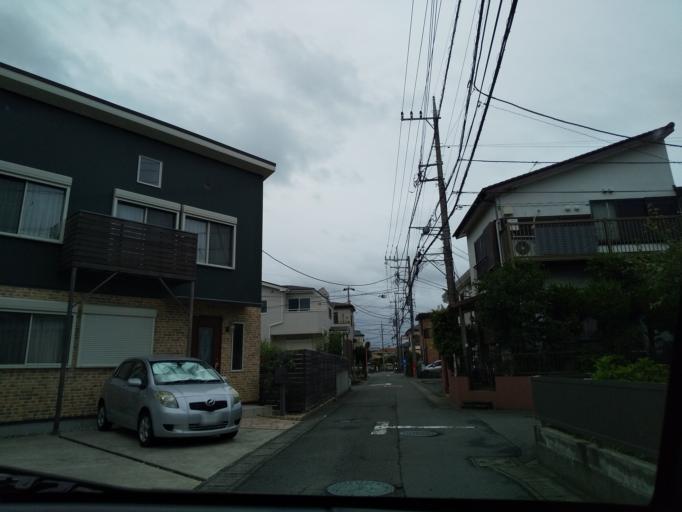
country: JP
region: Kanagawa
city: Minami-rinkan
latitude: 35.4350
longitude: 139.4439
